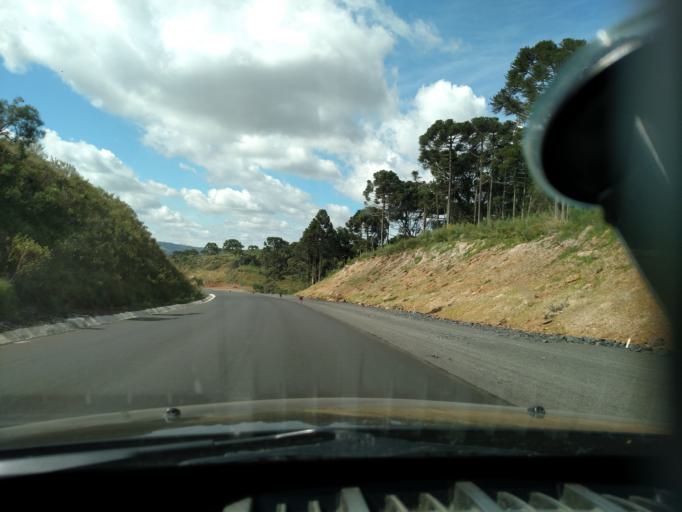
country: BR
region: Santa Catarina
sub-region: Sao Joaquim
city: Sao Joaquim
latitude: -28.0750
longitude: -50.0724
